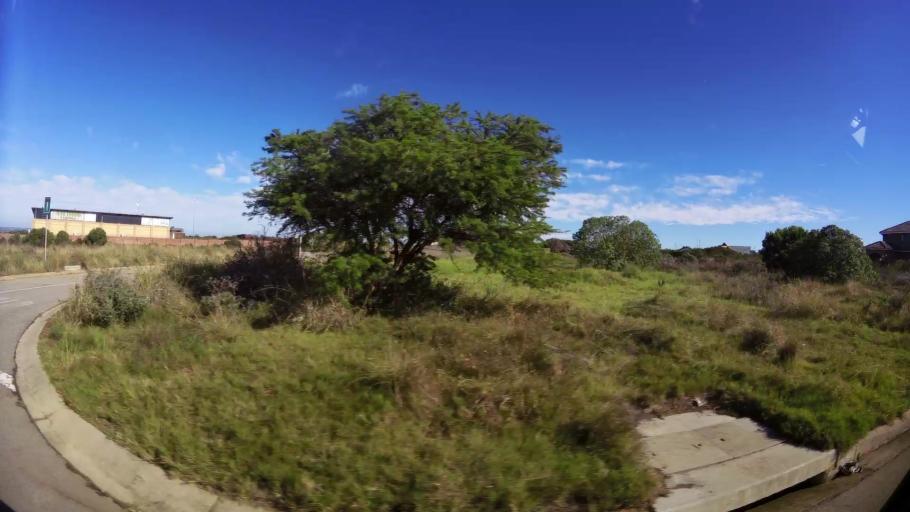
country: ZA
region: Eastern Cape
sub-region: Cacadu District Municipality
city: Jeffrey's Bay
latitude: -34.0389
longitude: 24.9079
